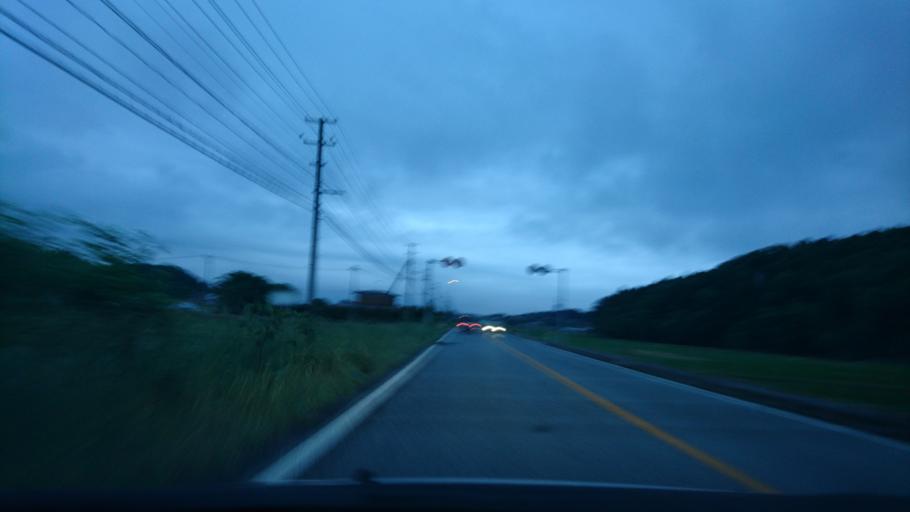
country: JP
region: Iwate
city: Ichinoseki
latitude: 38.8234
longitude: 141.0792
